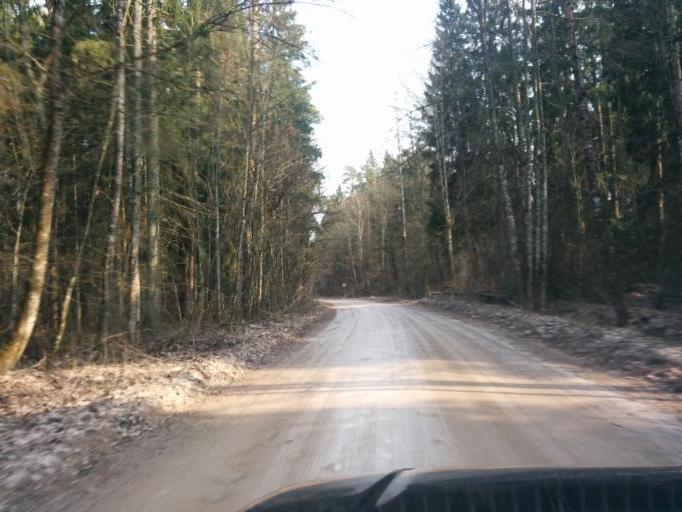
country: LV
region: Olaine
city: Olaine
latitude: 56.7904
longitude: 24.0301
